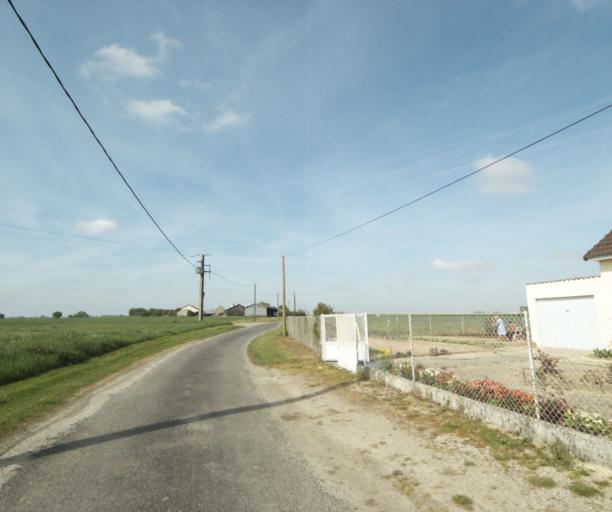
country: FR
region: Ile-de-France
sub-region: Departement de Seine-et-Marne
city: Nangis
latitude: 48.5749
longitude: 3.0384
